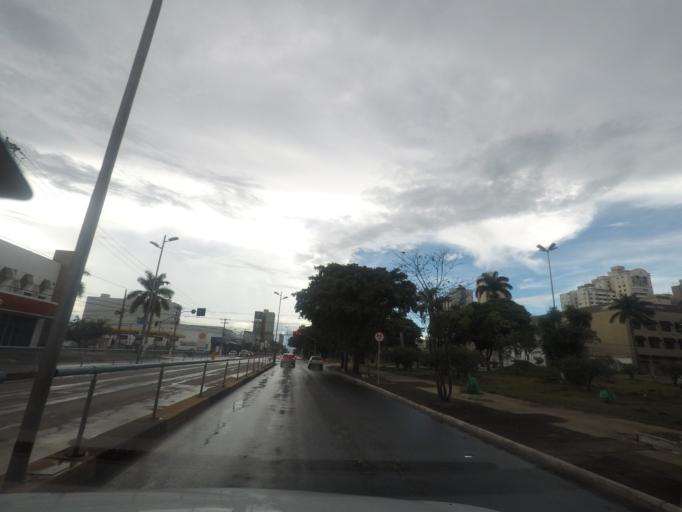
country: BR
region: Goias
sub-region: Goiania
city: Goiania
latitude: -16.6779
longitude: -49.2683
